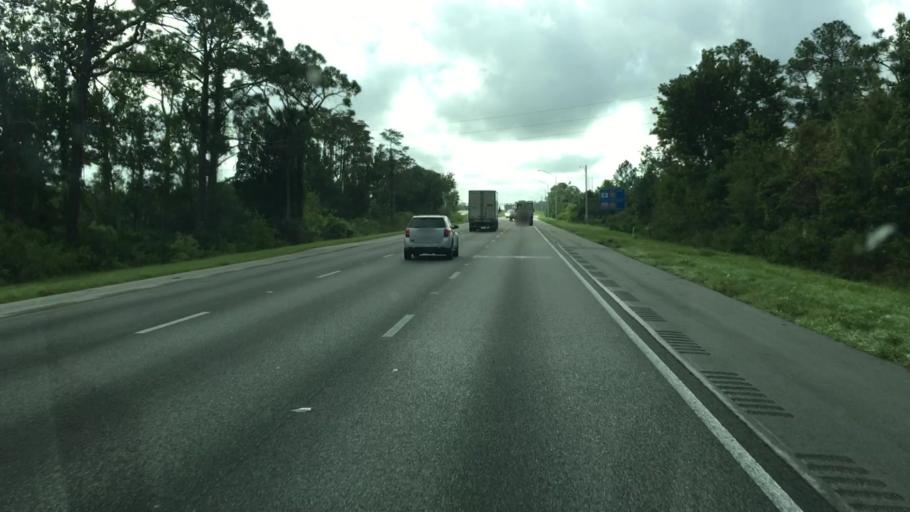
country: US
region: Florida
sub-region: Volusia County
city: Glencoe
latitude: 29.0204
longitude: -80.9932
